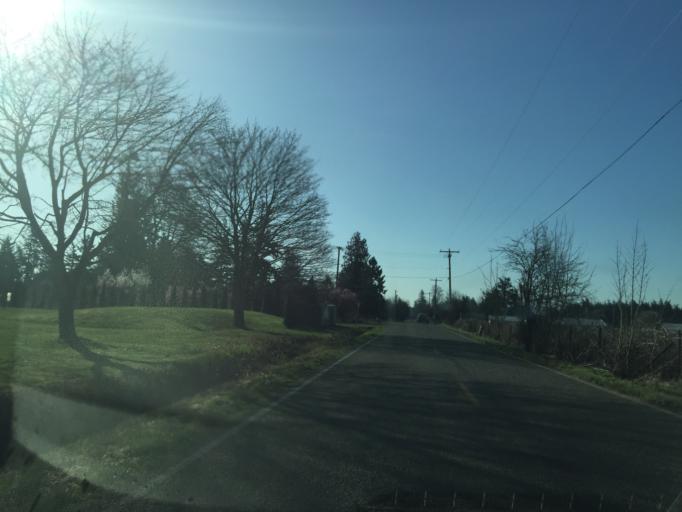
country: US
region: Washington
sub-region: Whatcom County
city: Lynden
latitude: 48.8679
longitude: -122.4969
